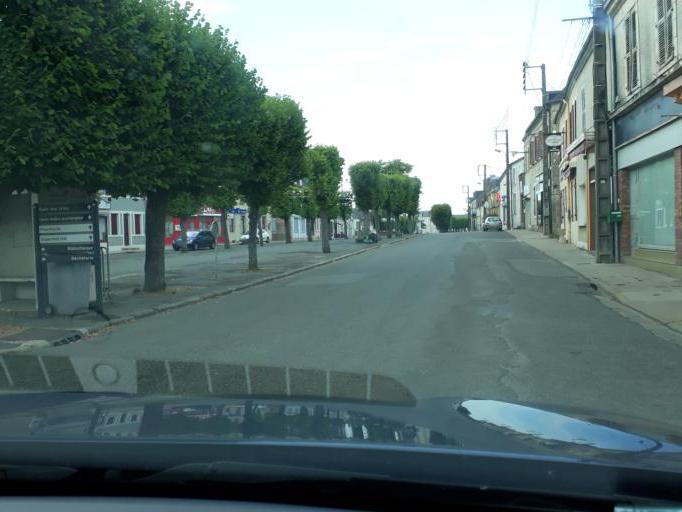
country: FR
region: Centre
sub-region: Departement du Cher
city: Baugy
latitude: 47.0812
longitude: 2.7279
